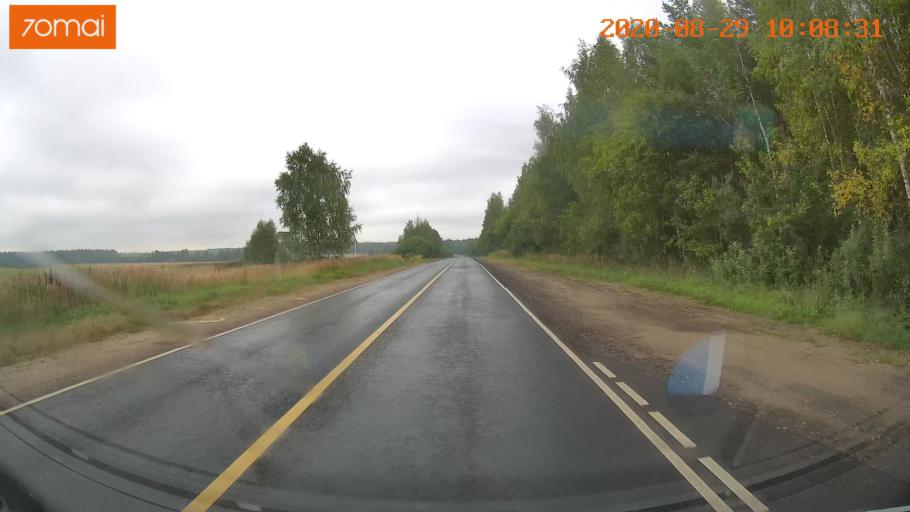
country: RU
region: Ivanovo
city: Kuznechikha
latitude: 57.3758
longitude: 42.5921
